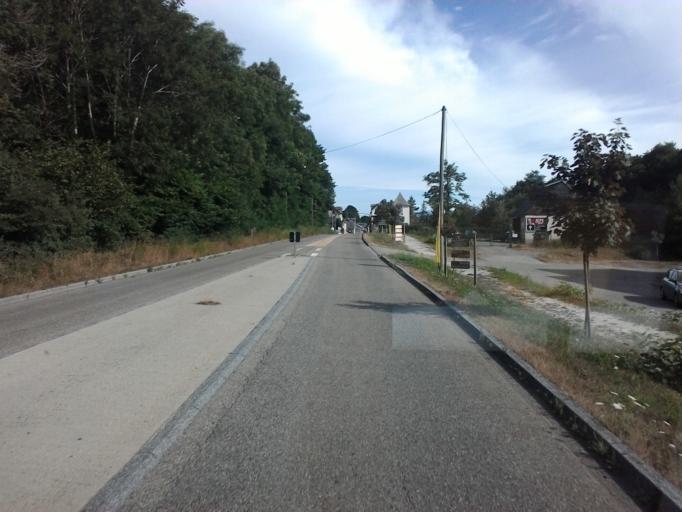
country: FR
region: Rhone-Alpes
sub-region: Departement de l'Isere
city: Notre-Dame-de-Mesage
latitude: 45.0213
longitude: 5.7746
